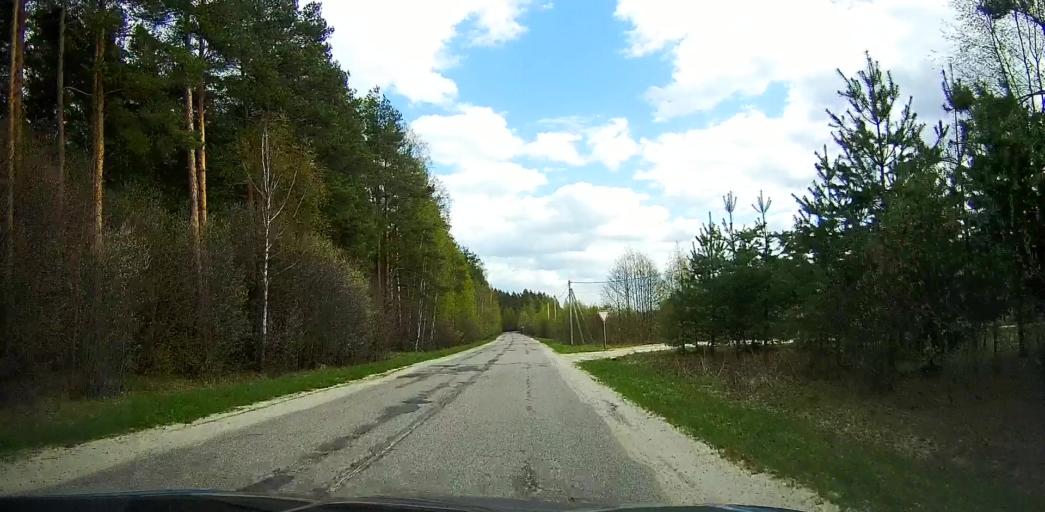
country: RU
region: Moskovskaya
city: Davydovo
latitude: 55.6458
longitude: 38.7694
